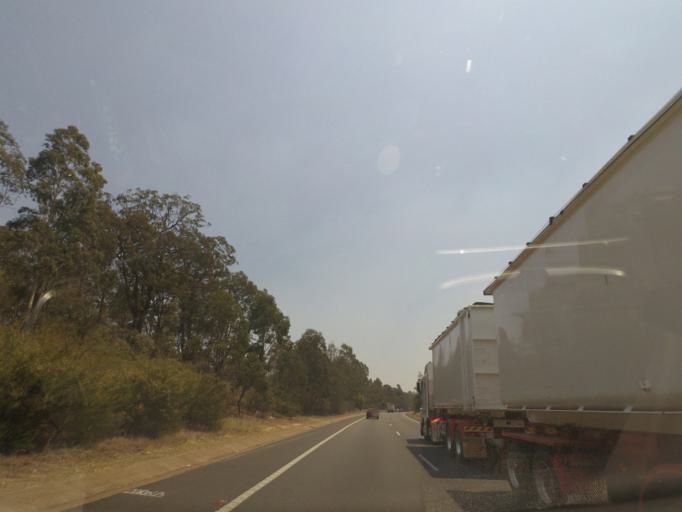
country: AU
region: New South Wales
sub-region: Newcastle
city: Beresfield
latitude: -32.8297
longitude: 151.6333
